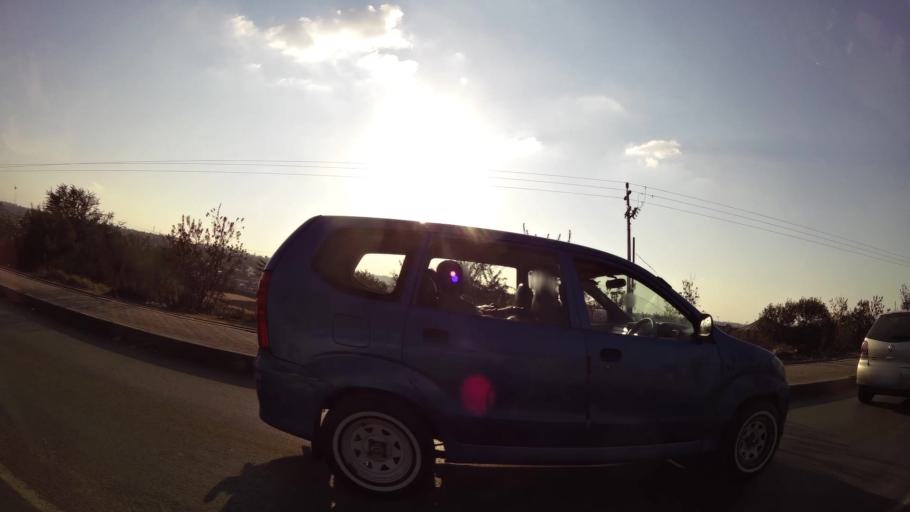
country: ZA
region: Gauteng
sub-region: Ekurhuleni Metropolitan Municipality
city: Tembisa
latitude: -25.9983
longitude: 28.1969
